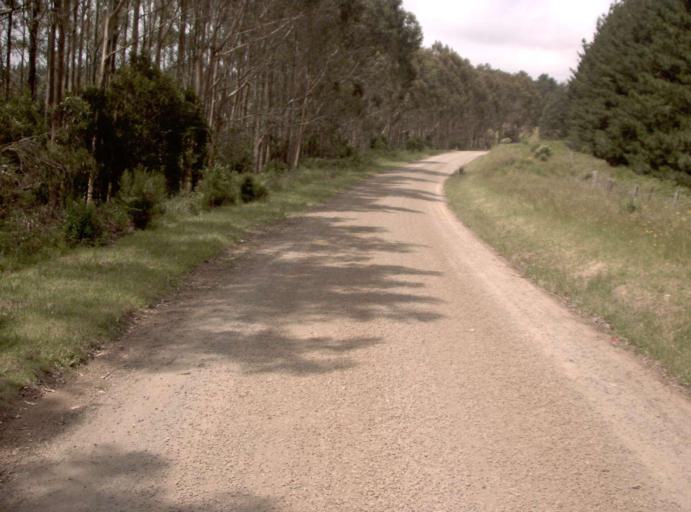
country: AU
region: Victoria
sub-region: Latrobe
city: Traralgon
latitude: -38.4045
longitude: 146.6414
